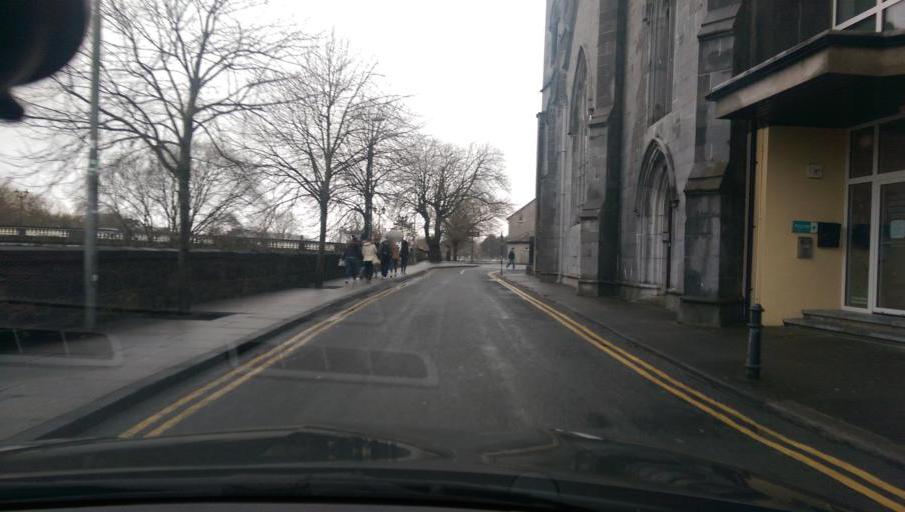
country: IE
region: Connaught
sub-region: County Galway
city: Gaillimh
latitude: 53.2750
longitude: -9.0551
